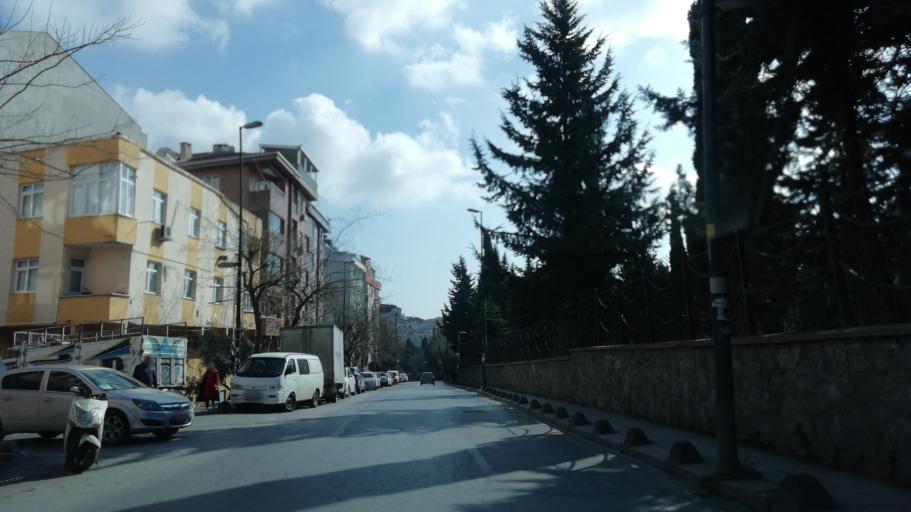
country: TR
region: Istanbul
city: Bahcelievler
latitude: 41.0167
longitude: 28.8368
